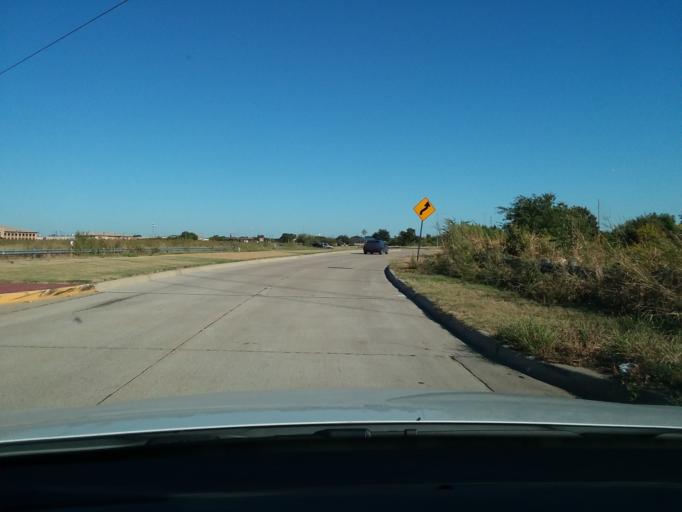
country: US
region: Texas
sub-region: Denton County
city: Lewisville
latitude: 33.0656
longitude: -97.0205
